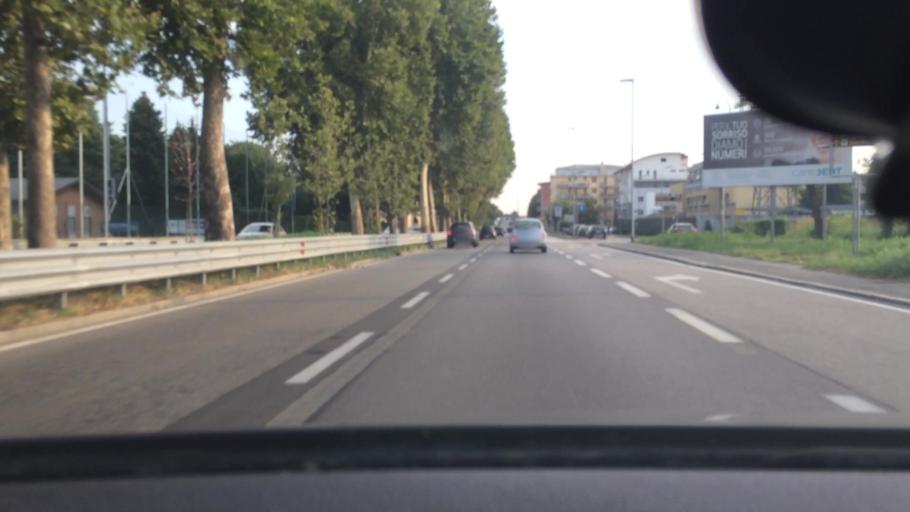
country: IT
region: Lombardy
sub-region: Provincia di Bergamo
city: Gorle
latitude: 45.6975
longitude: 9.6946
